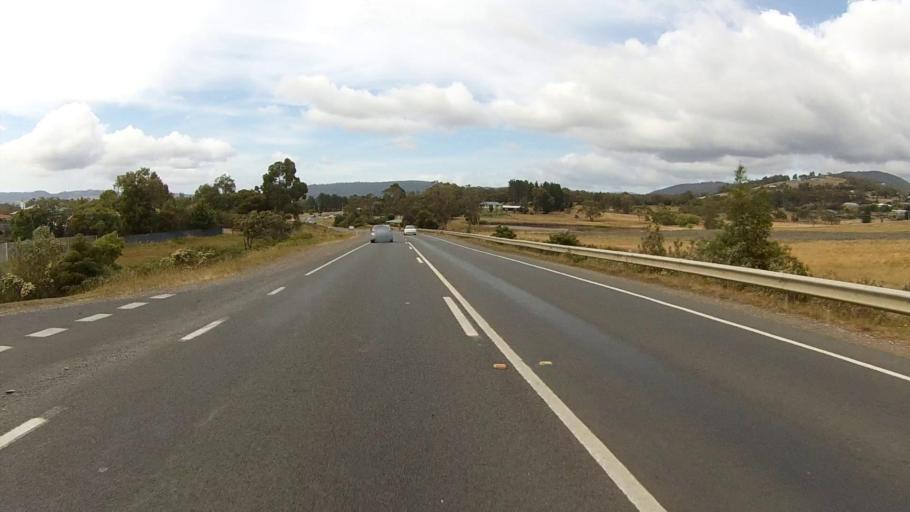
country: AU
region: Tasmania
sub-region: Kingborough
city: Margate
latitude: -43.0306
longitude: 147.2640
